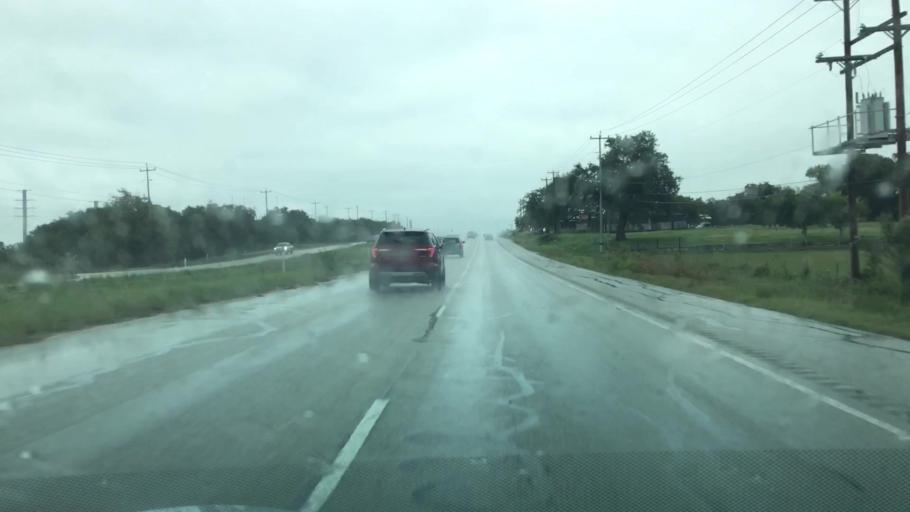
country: US
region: Texas
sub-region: Comal County
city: Bulverde
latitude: 29.7271
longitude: -98.4410
